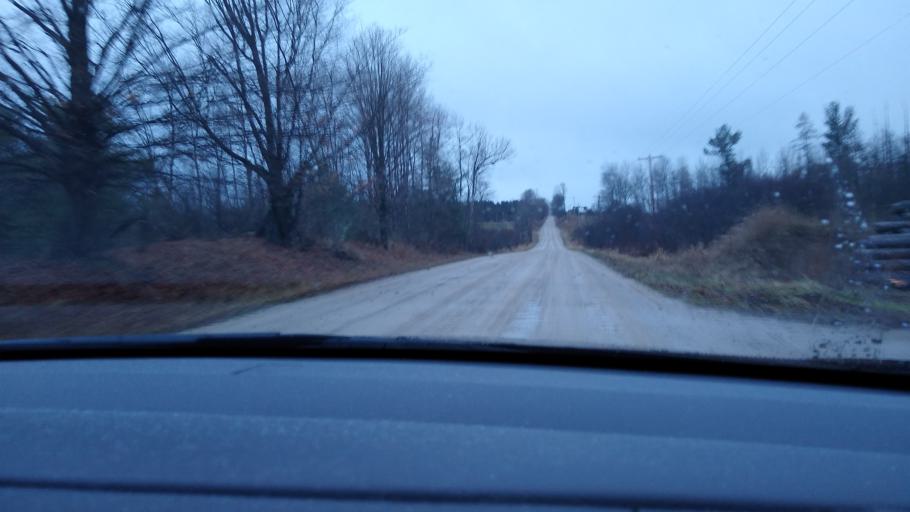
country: US
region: Michigan
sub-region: Wexford County
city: Cadillac
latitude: 44.1744
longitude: -85.3953
